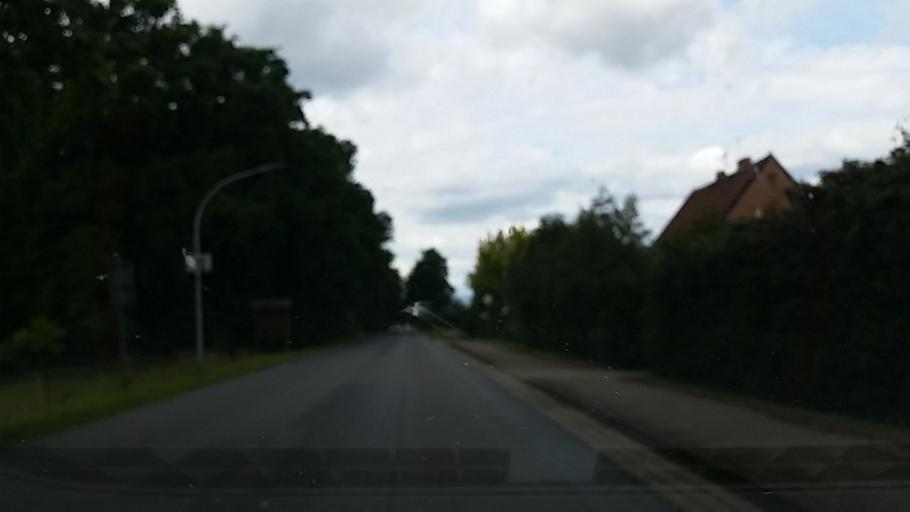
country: DE
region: Lower Saxony
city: Ribbesbuttel
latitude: 52.4341
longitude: 10.5044
